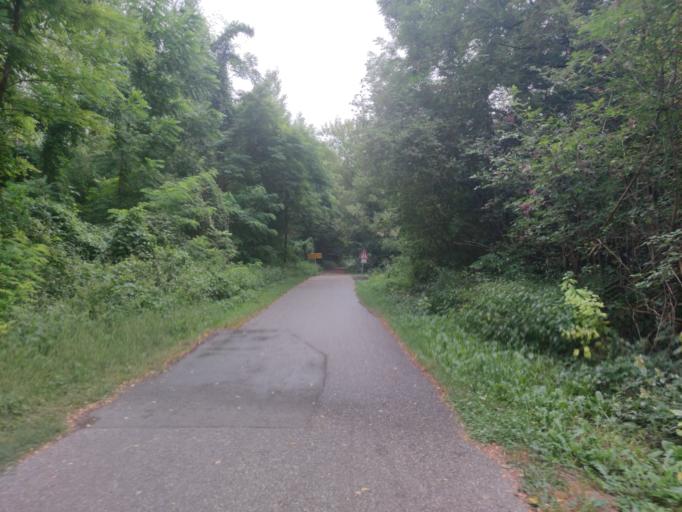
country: AT
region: Lower Austria
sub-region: Politischer Bezirk Korneuburg
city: Korneuburg
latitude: 48.3435
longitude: 16.3142
